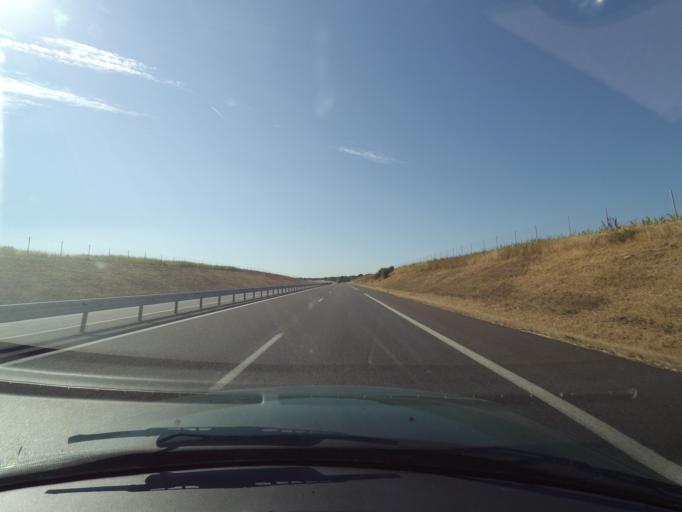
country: FR
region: Poitou-Charentes
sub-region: Departement de la Vienne
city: Terce
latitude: 46.4694
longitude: 0.5440
